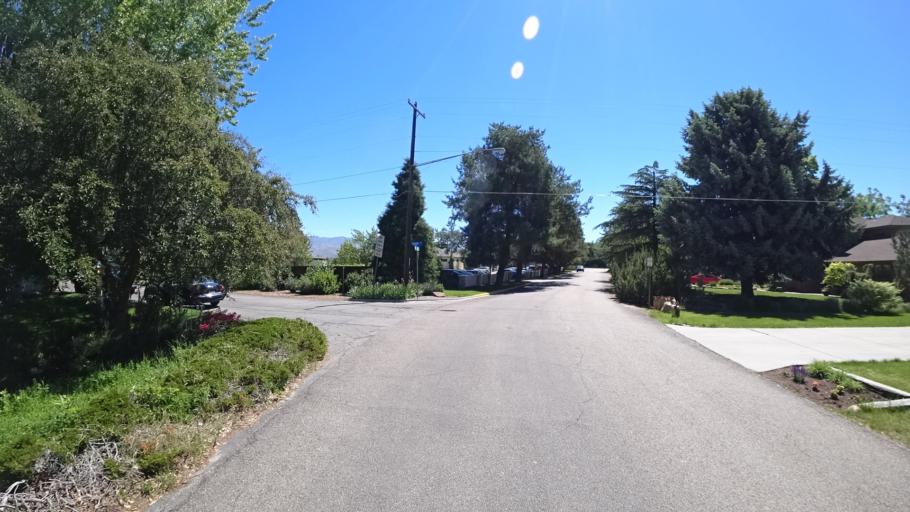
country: US
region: Idaho
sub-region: Ada County
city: Garden City
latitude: 43.5861
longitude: -116.2412
